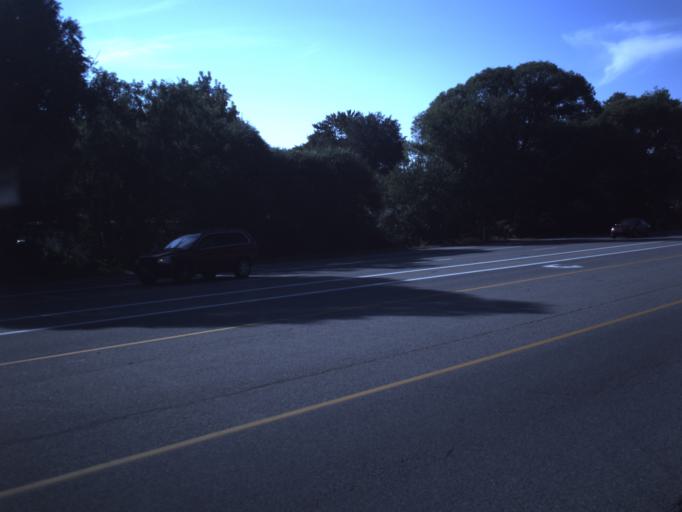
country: US
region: Utah
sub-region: Salt Lake County
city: Holladay
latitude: 40.6595
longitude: -111.8548
